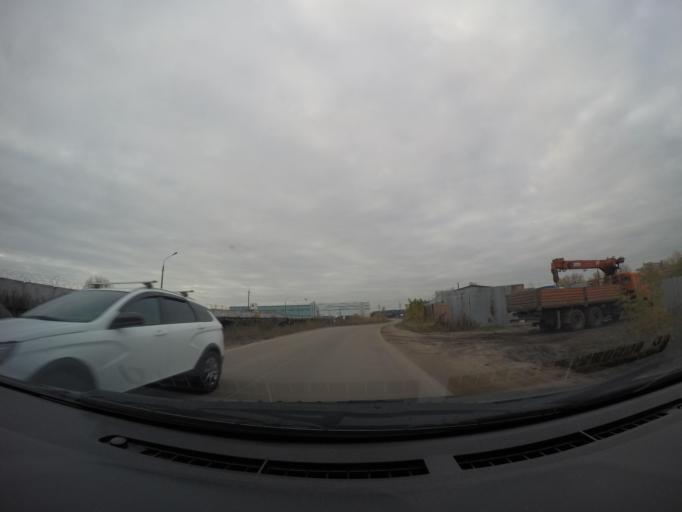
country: RU
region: Moskovskaya
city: Staraya Kupavna
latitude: 55.7938
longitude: 38.1835
